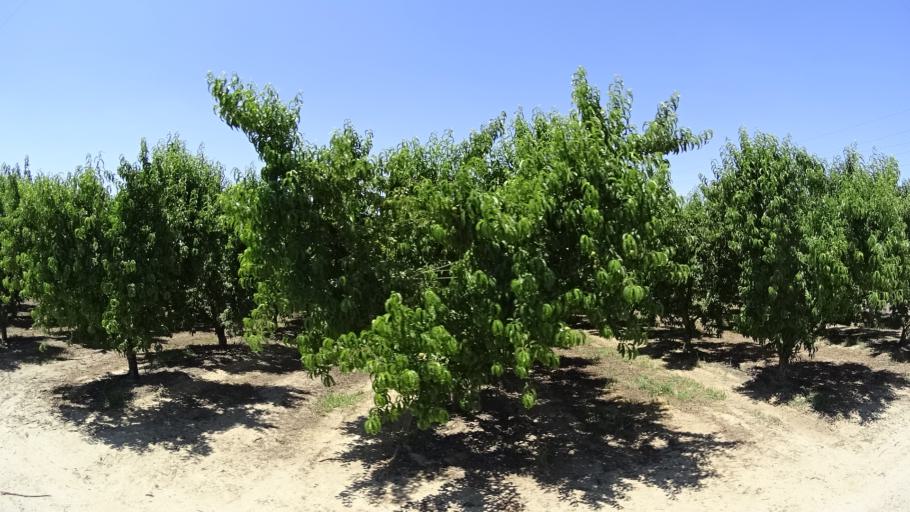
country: US
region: California
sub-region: Fresno County
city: Kingsburg
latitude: 36.4867
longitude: -119.5910
